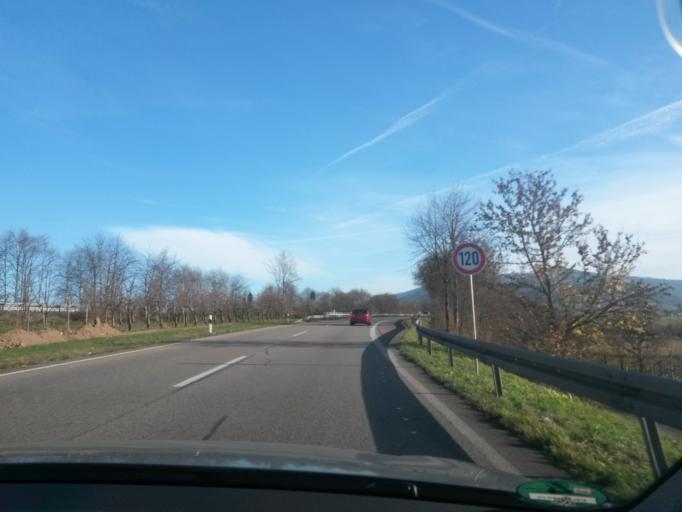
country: DE
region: Baden-Wuerttemberg
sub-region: Freiburg Region
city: Denzlingen
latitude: 48.0586
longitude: 7.8737
